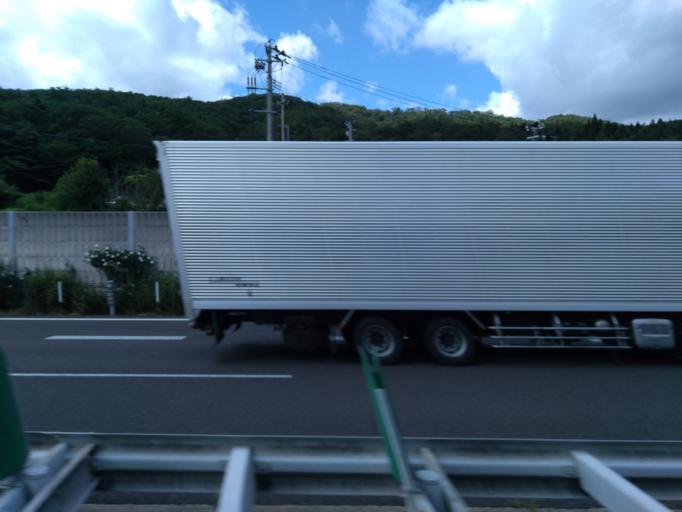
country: JP
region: Miyagi
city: Sendai
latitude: 38.2859
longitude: 140.8087
